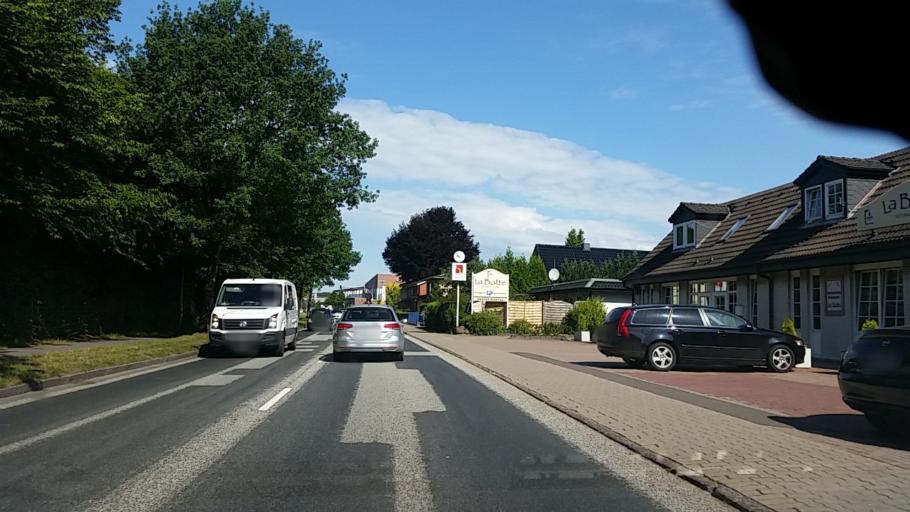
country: DE
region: Schleswig-Holstein
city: Kaltenkirchen
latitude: 53.8326
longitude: 9.9698
